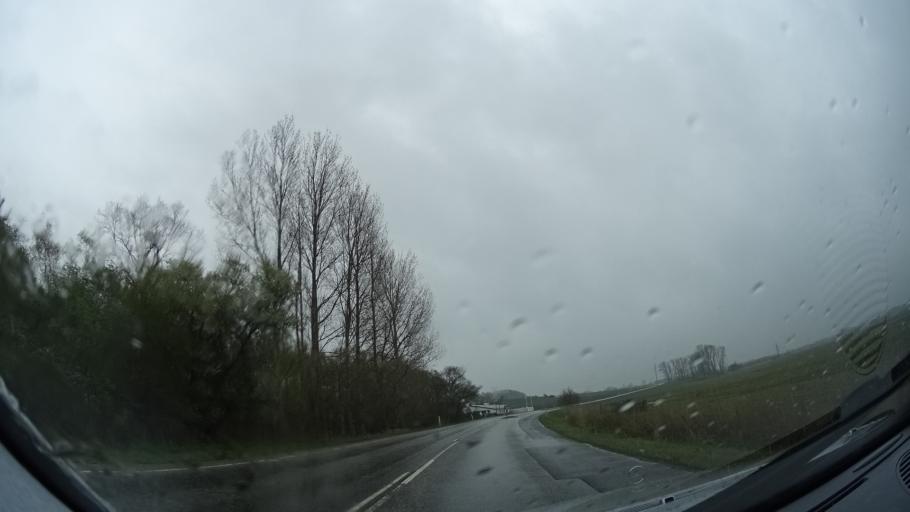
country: DK
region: Zealand
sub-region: Holbaek Kommune
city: Holbaek
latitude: 55.7608
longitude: 11.6295
